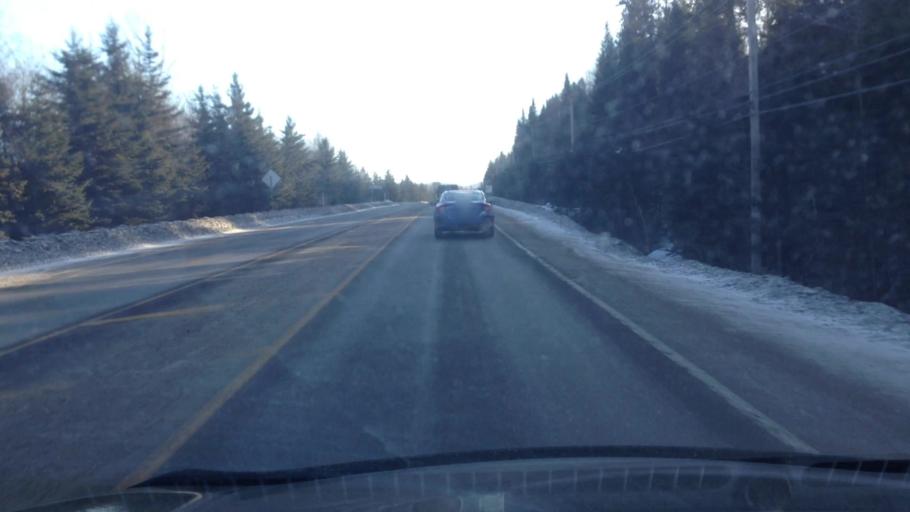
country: CA
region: Quebec
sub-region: Laurentides
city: Saint-Sauveur
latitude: 45.8985
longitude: -74.2114
